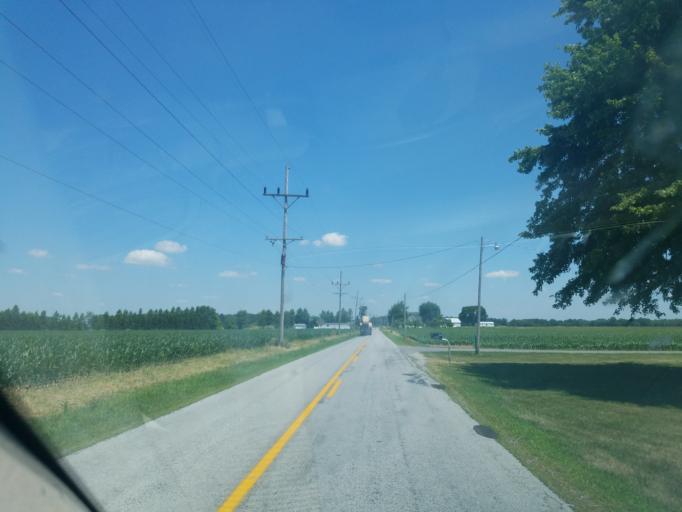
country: US
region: Ohio
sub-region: Allen County
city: Delphos
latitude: 40.7801
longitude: -84.3073
